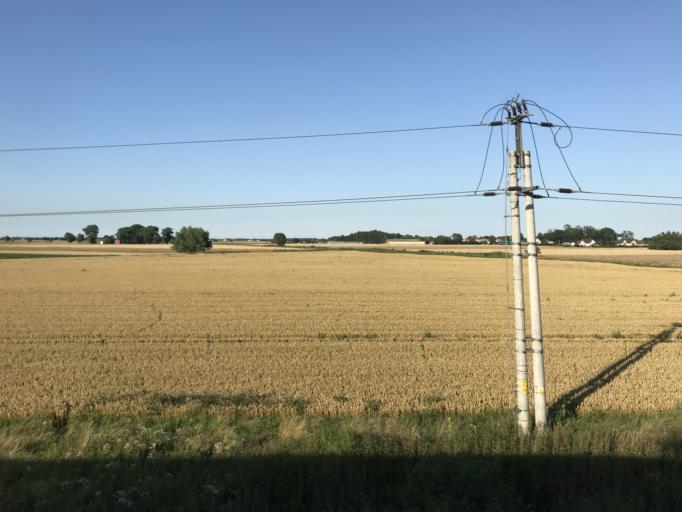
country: PL
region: Pomeranian Voivodeship
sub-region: Powiat tczewski
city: Tczew
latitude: 54.1199
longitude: 18.7677
